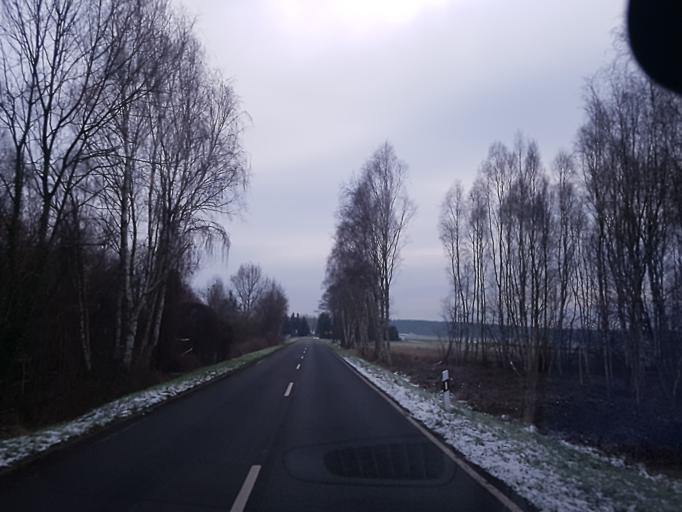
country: DE
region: Brandenburg
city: Crinitz
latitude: 51.7376
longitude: 13.8456
